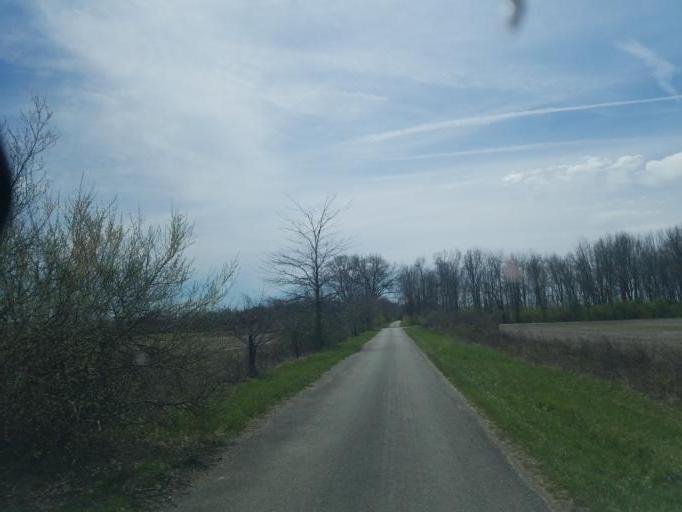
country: US
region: Ohio
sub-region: Delaware County
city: Ashley
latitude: 40.4245
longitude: -83.0398
